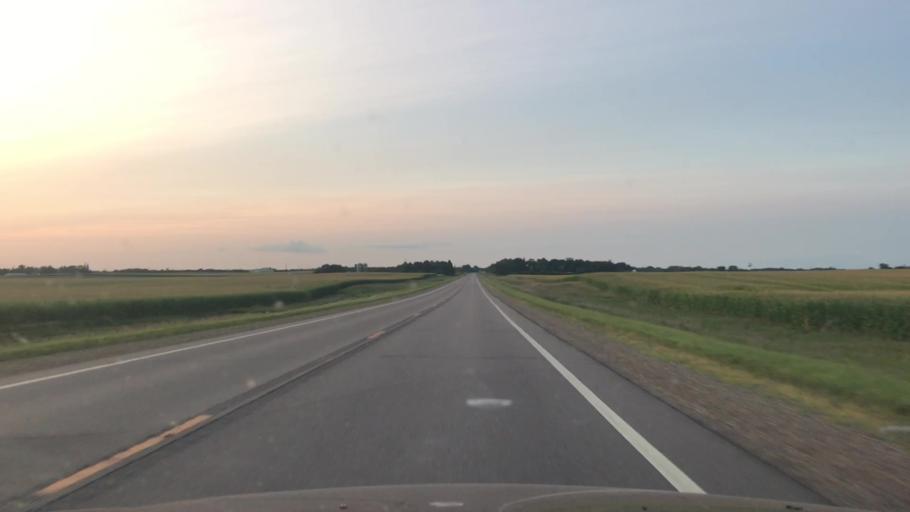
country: US
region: Minnesota
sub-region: Redwood County
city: Redwood Falls
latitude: 44.5089
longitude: -95.1179
